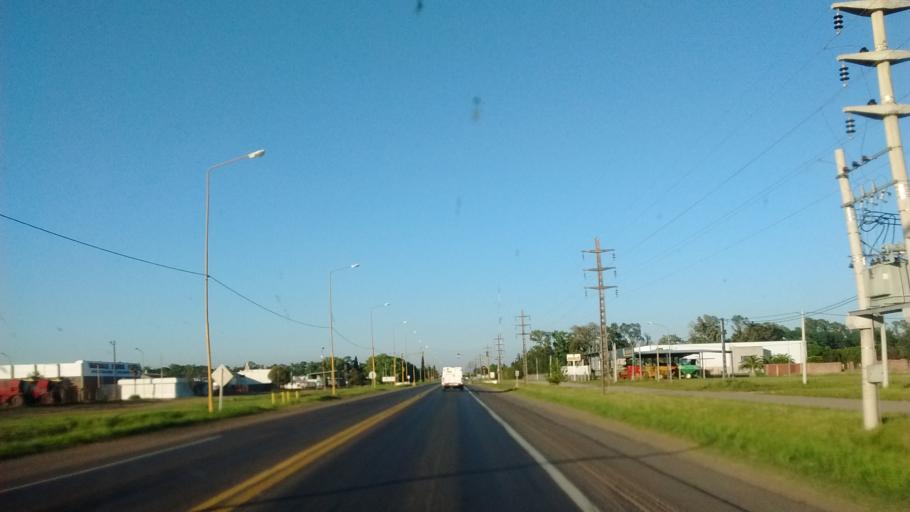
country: AR
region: Santa Fe
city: Firmat
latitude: -33.4531
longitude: -61.4972
